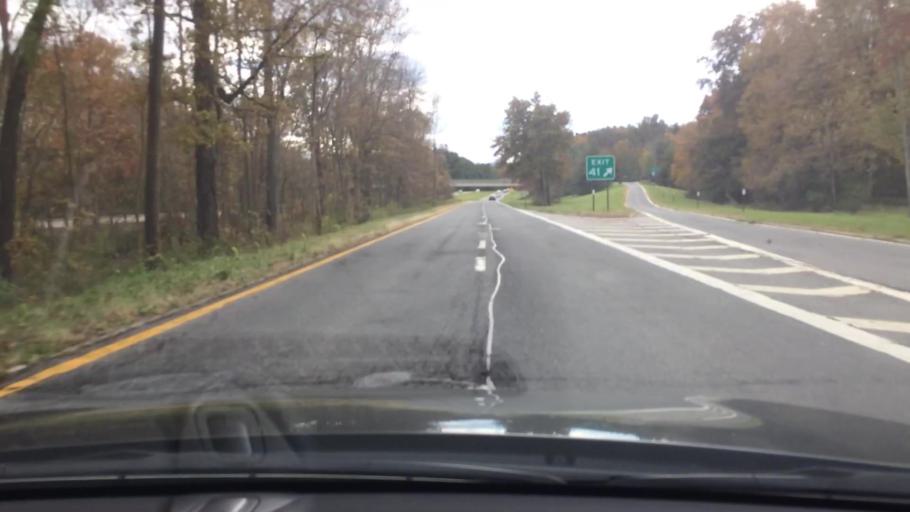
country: US
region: New York
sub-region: Dutchess County
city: Hillside Lake
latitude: 41.5979
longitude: -73.7642
